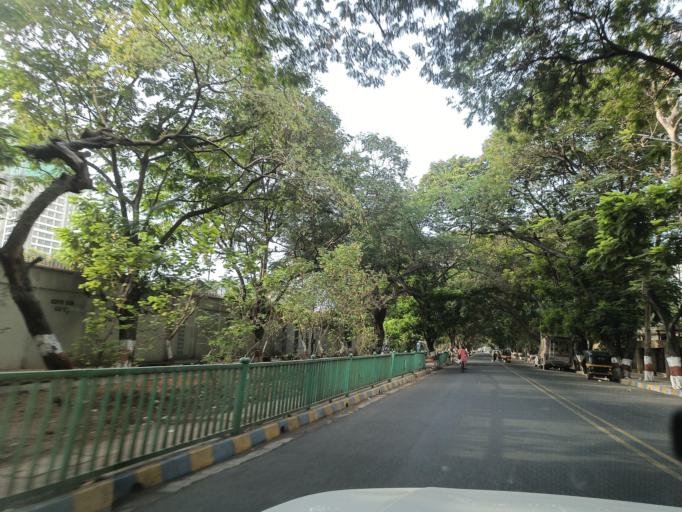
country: IN
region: Maharashtra
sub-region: Thane
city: Thane
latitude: 19.1869
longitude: 72.9638
